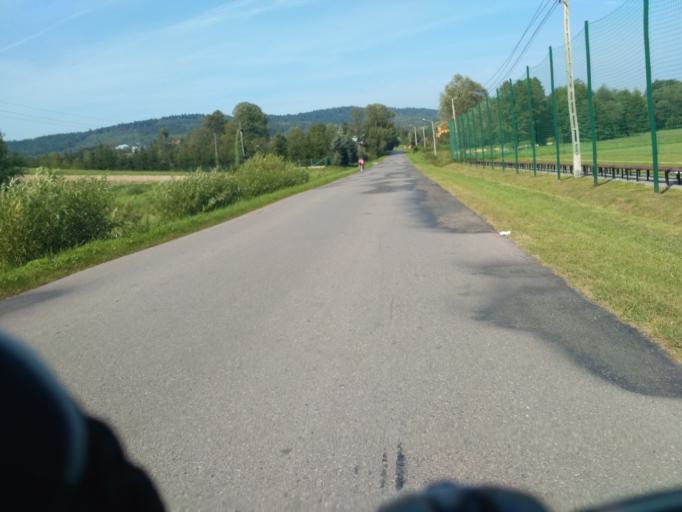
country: PL
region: Subcarpathian Voivodeship
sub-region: Powiat brzozowski
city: Golcowa
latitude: 49.7742
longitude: 22.0095
